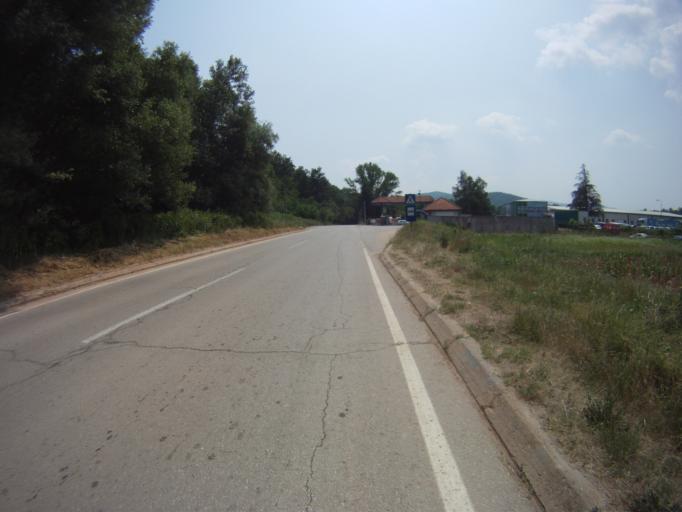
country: RS
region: Central Serbia
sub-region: Nisavski Okrug
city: Gadzin Han
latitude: 43.2306
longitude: 22.0310
